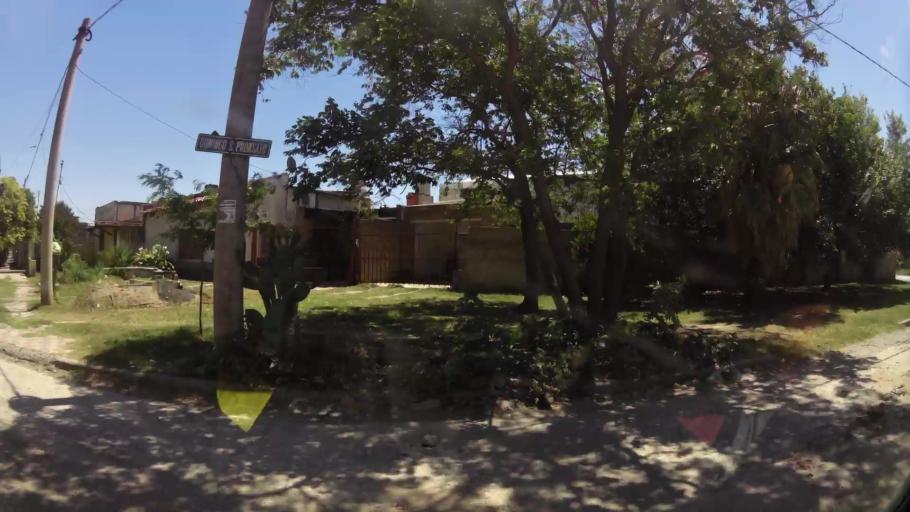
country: AR
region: Cordoba
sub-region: Departamento de Capital
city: Cordoba
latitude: -31.3901
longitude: -64.1479
